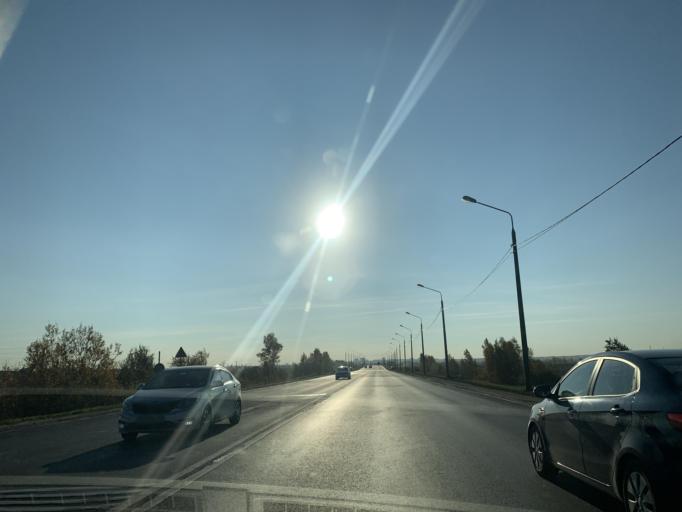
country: RU
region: Jaroslavl
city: Yaroslavl
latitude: 57.6324
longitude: 39.7503
